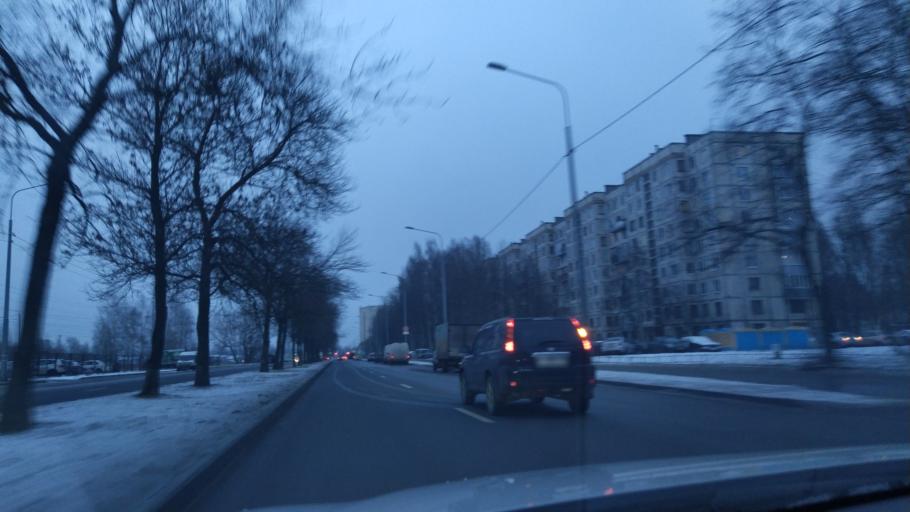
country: RU
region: St.-Petersburg
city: Grazhdanka
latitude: 60.0175
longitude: 30.4237
